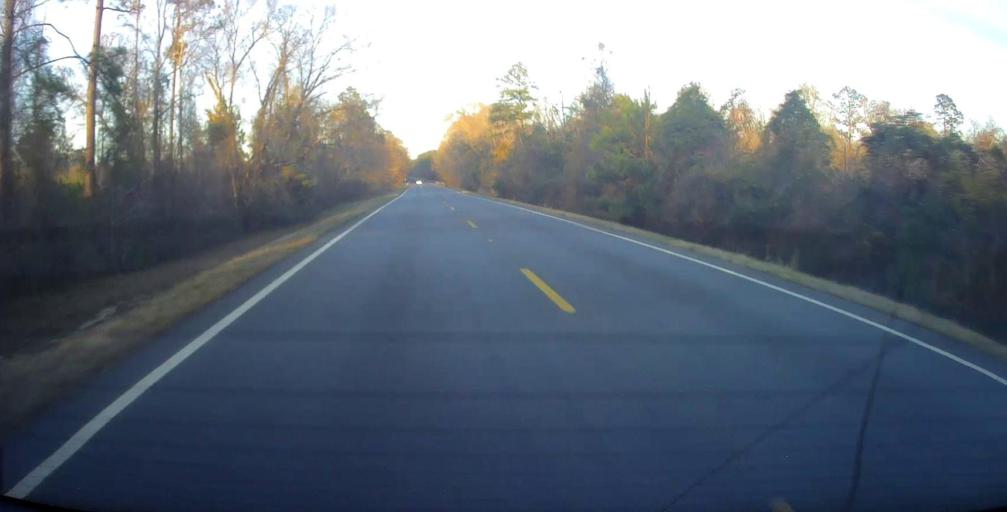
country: US
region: Georgia
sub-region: Dodge County
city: Chester
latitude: 32.3165
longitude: -83.0582
